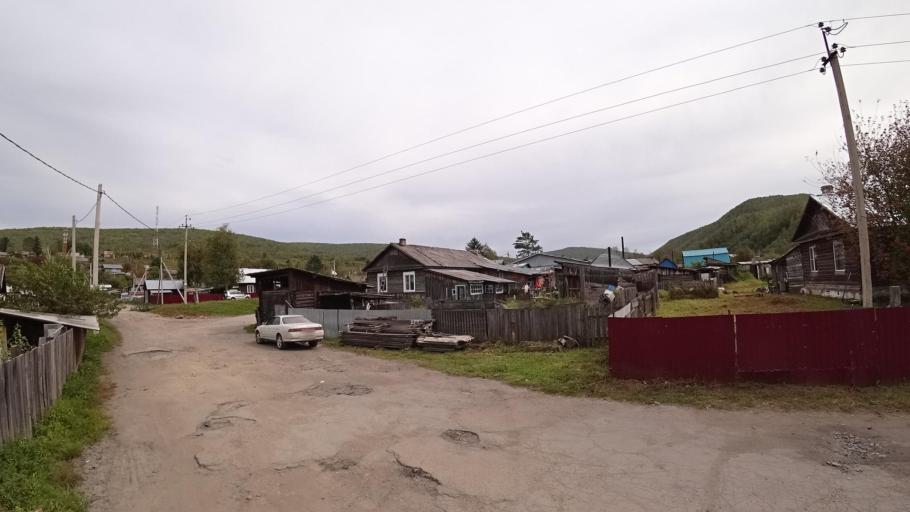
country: RU
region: Jewish Autonomous Oblast
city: Khingansk
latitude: 49.1257
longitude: 131.1997
